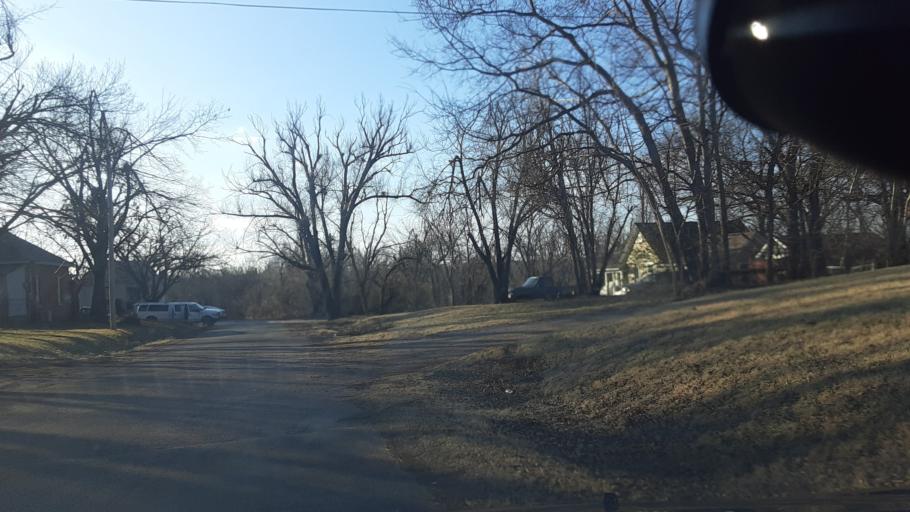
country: US
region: Oklahoma
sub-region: Logan County
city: Guthrie
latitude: 35.8822
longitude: -97.4258
